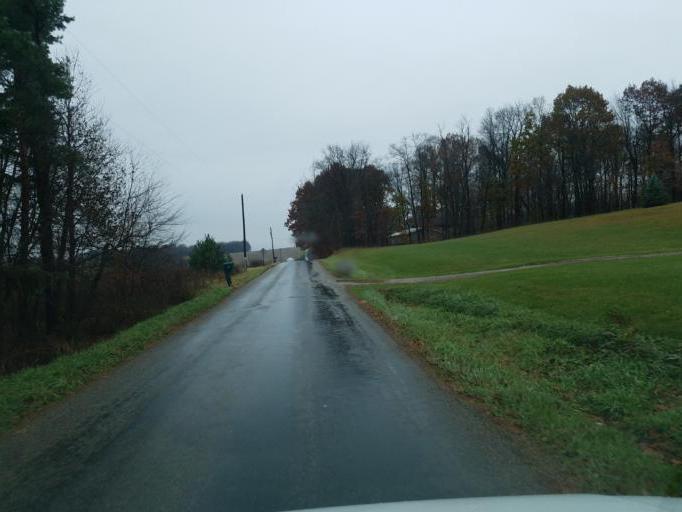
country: US
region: Ohio
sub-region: Sandusky County
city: Bellville
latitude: 40.5847
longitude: -82.5675
